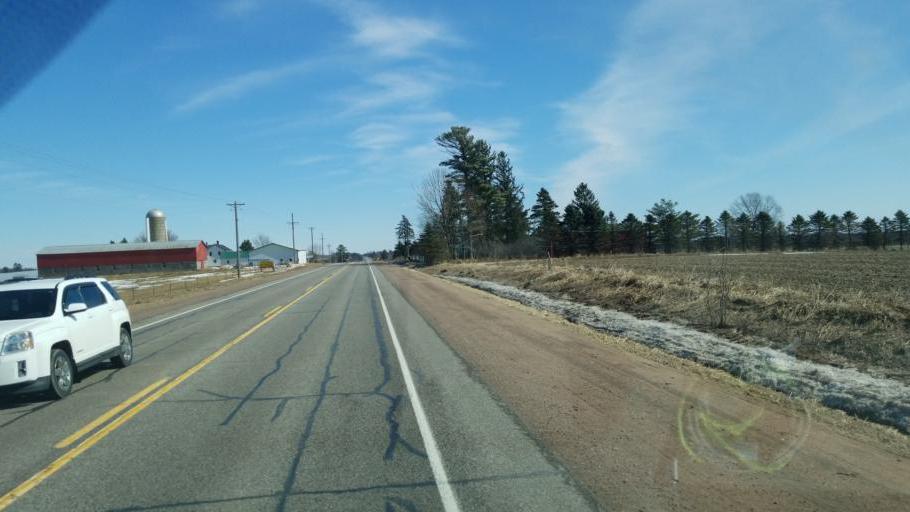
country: US
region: Wisconsin
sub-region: Clark County
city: Loyal
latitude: 44.5822
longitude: -90.4214
